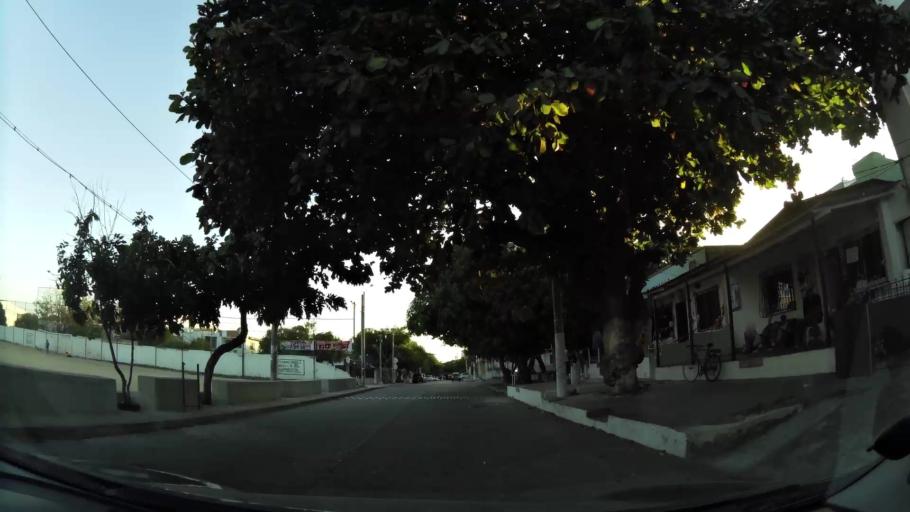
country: CO
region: Atlantico
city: Barranquilla
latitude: 10.9783
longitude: -74.8050
